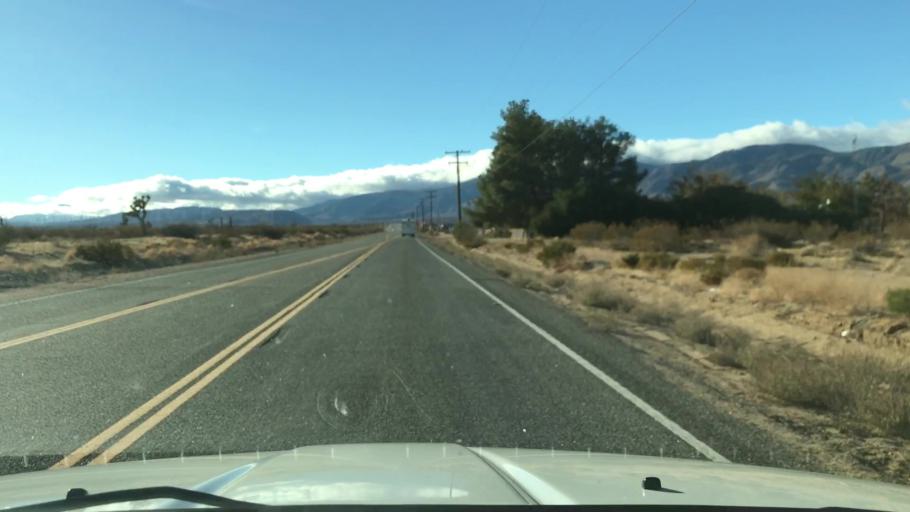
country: US
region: California
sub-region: Kern County
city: Mojave
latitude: 35.1255
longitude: -118.1117
